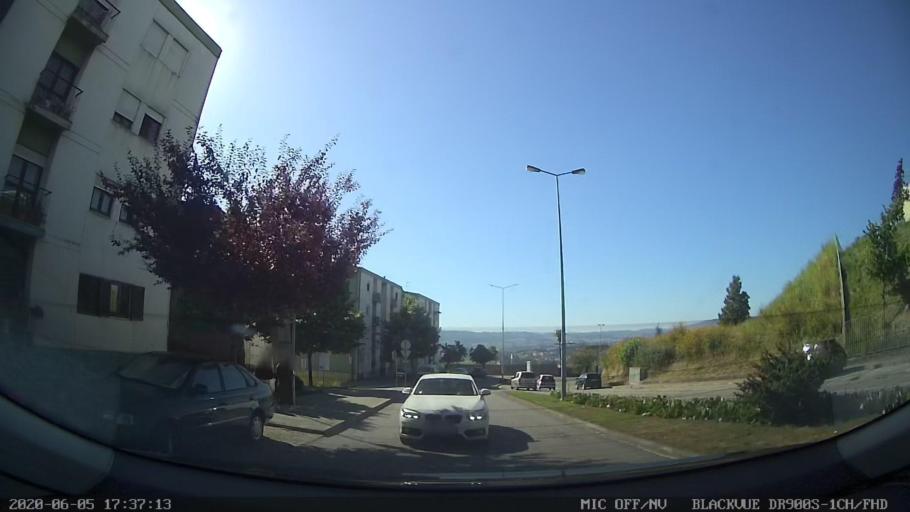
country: PT
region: Porto
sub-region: Penafiel
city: Penafiel
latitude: 41.2085
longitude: -8.2823
